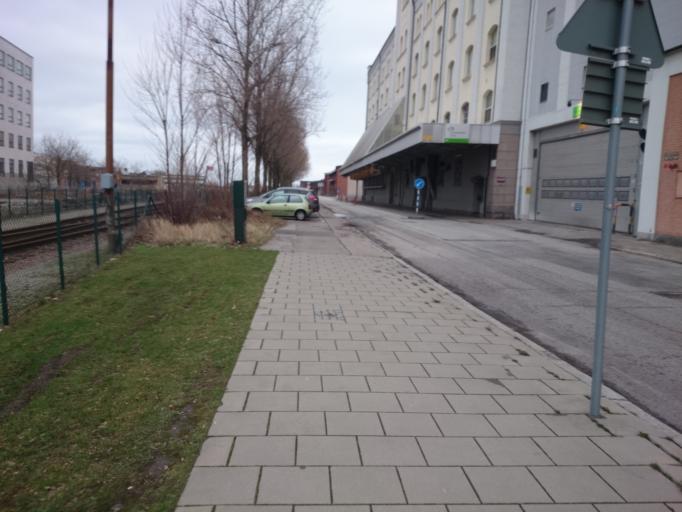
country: SE
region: Skane
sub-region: Malmo
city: Malmoe
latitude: 55.6082
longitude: 12.9905
